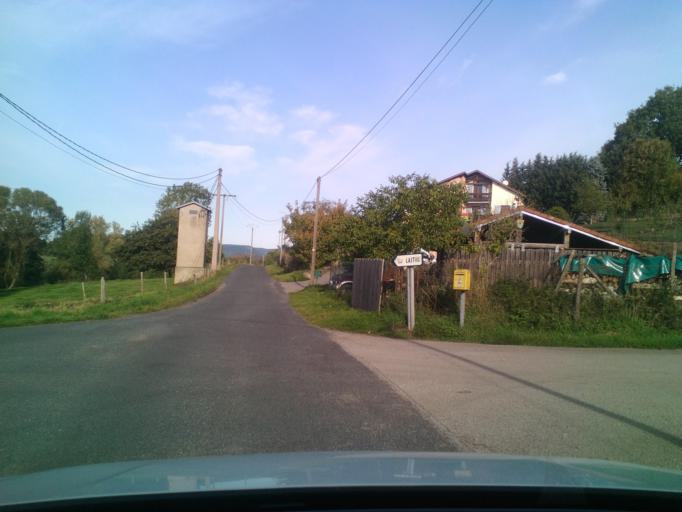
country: FR
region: Lorraine
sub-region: Departement des Vosges
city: Senones
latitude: 48.3527
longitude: 7.0212
